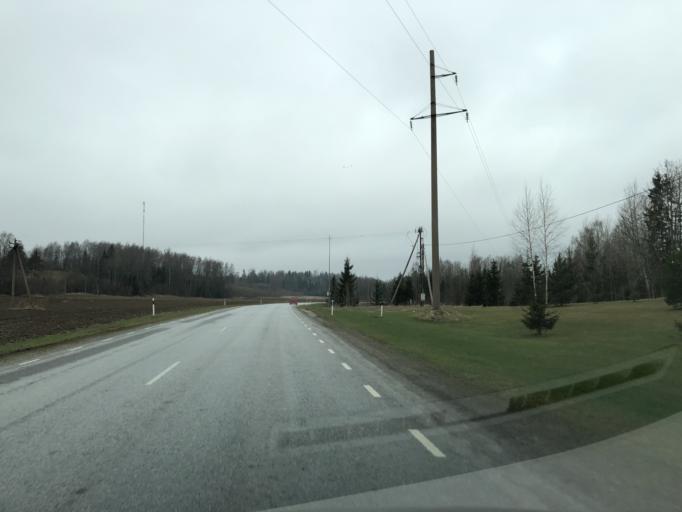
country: EE
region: Laeaene-Virumaa
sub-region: Rakke vald
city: Rakke
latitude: 58.9709
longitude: 26.2714
